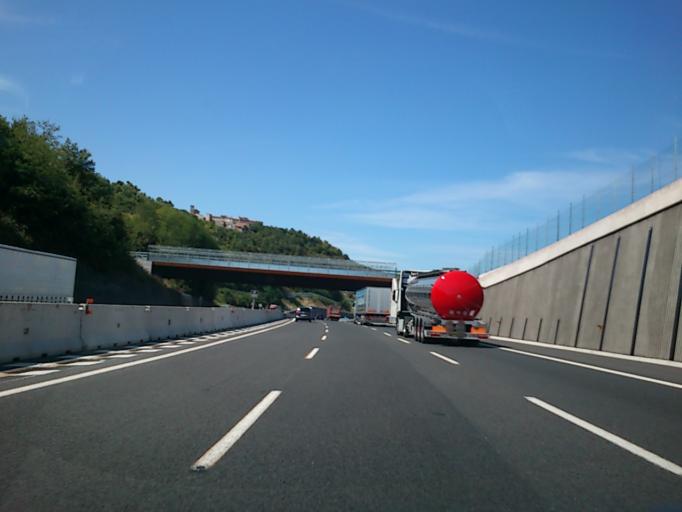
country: IT
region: The Marches
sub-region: Provincia di Pesaro e Urbino
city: Fenile
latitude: 43.8587
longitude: 12.9413
